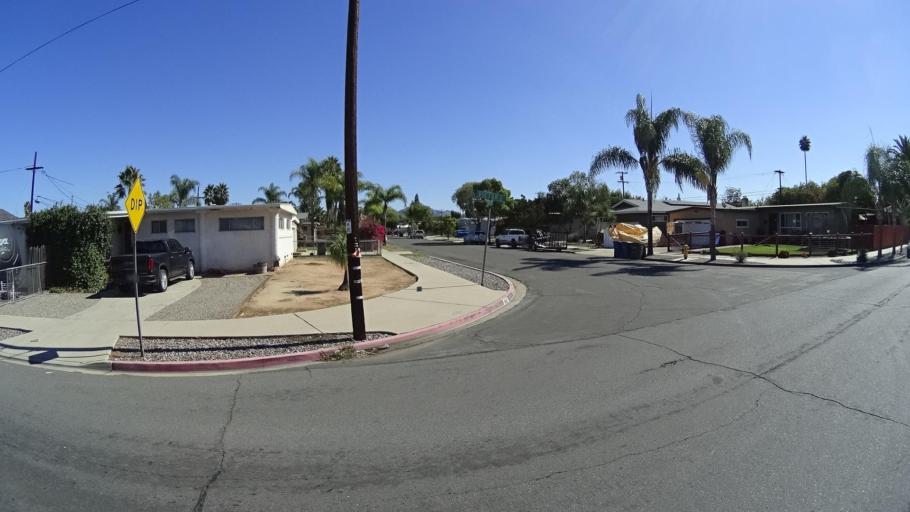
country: US
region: California
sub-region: San Diego County
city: El Cajon
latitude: 32.8102
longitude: -116.9553
